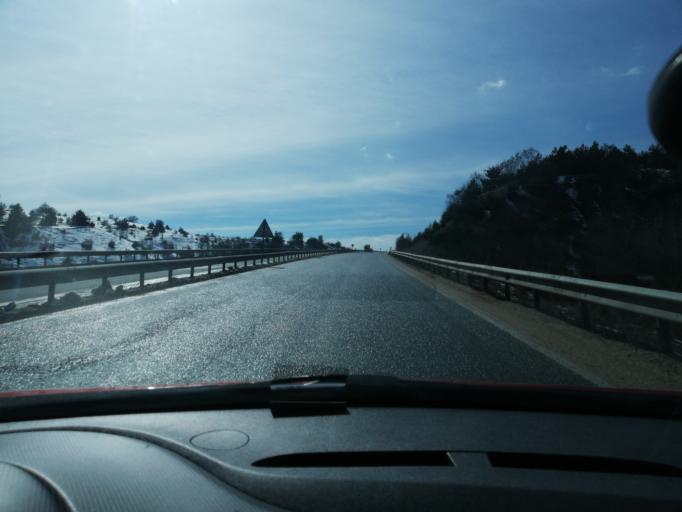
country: TR
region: Karabuk
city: Gozyeri
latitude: 40.8312
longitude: 32.3919
